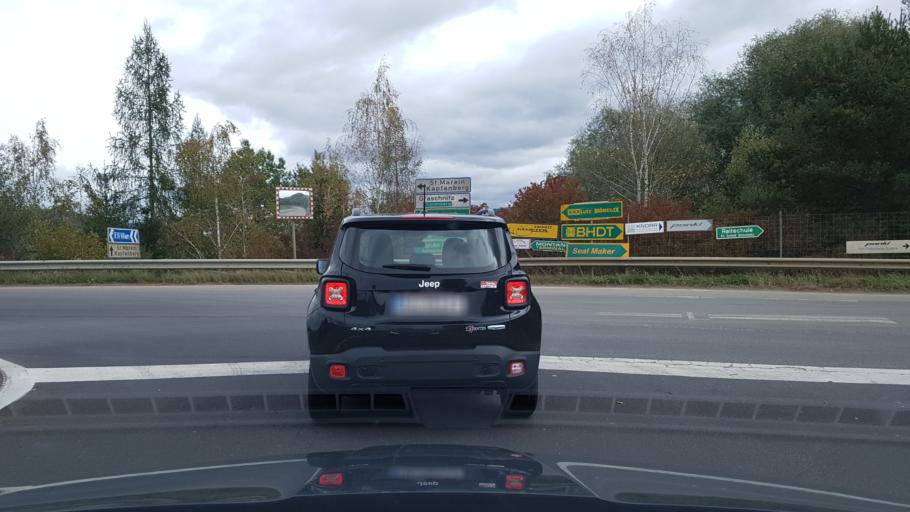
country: AT
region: Styria
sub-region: Politischer Bezirk Bruck-Muerzzuschlag
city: Sankt Marein im Muerztal
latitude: 47.4632
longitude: 15.3549
